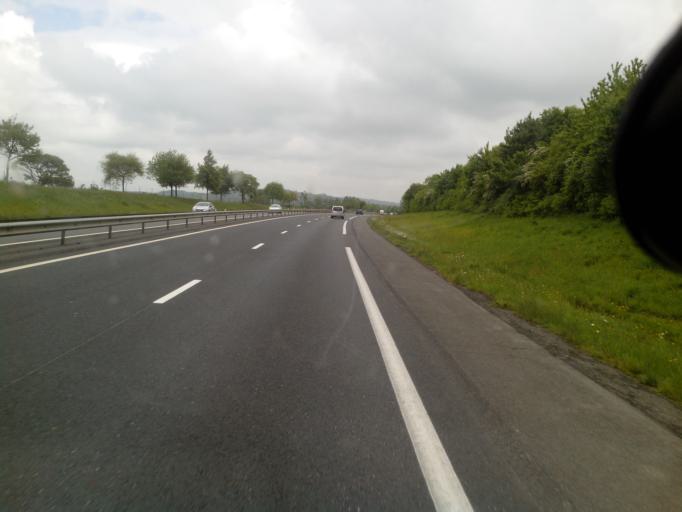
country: FR
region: Lower Normandy
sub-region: Departement du Calvados
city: Saint-Martin-des-Besaces
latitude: 49.0149
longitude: -0.8682
